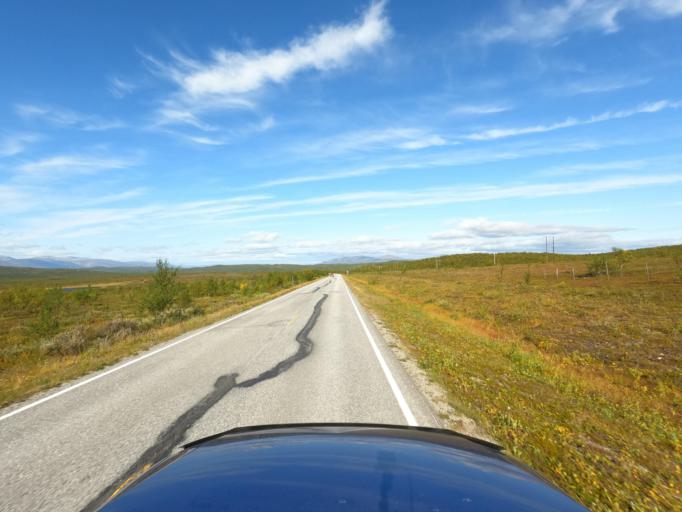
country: NO
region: Finnmark Fylke
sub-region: Karasjok
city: Karasjohka
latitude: 69.7299
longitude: 25.2343
